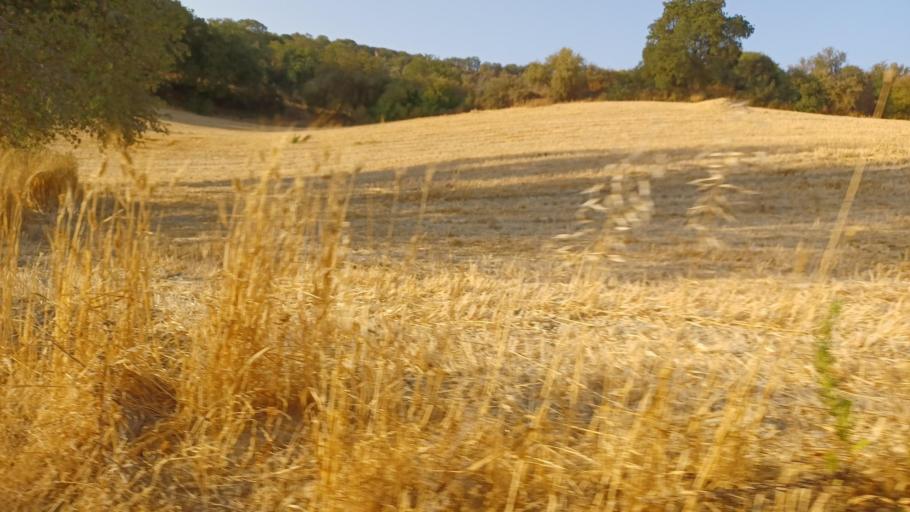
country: CY
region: Pafos
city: Polis
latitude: 34.9495
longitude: 32.4785
